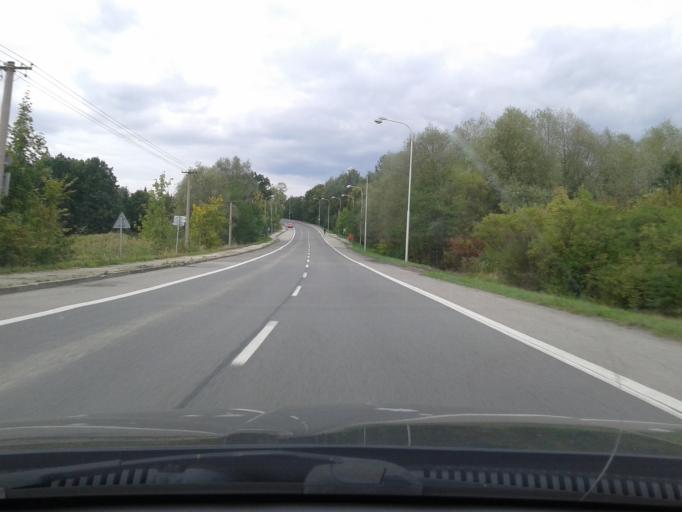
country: CZ
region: Moravskoslezsky
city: Orlova
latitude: 49.8546
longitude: 18.4495
